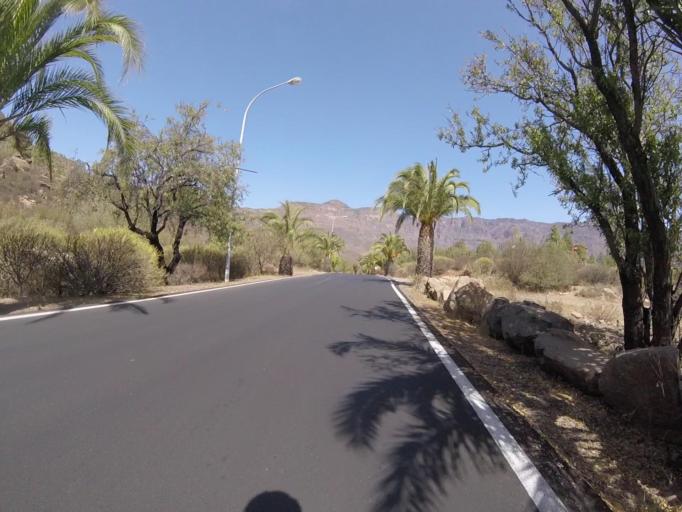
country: ES
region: Canary Islands
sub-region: Provincia de Las Palmas
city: San Bartolome
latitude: 27.9169
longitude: -15.5748
